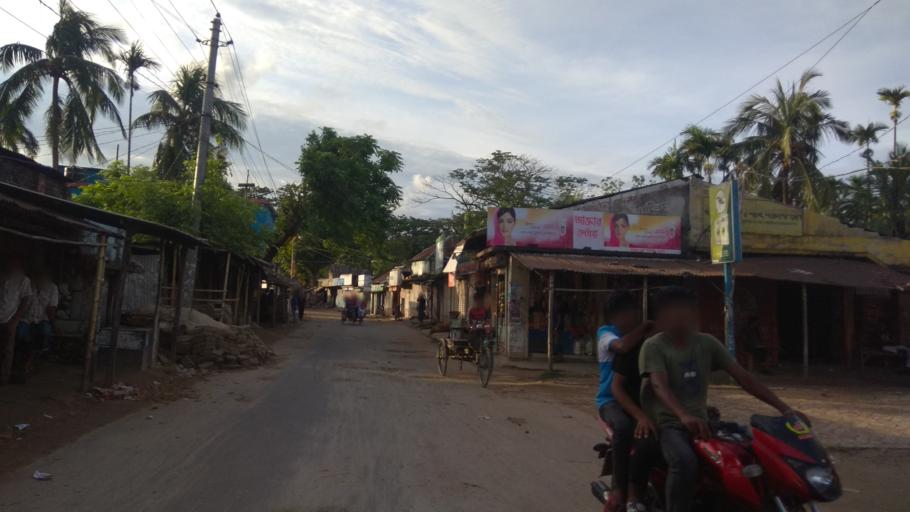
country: BD
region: Khulna
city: Kalia
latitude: 23.0383
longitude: 89.6325
